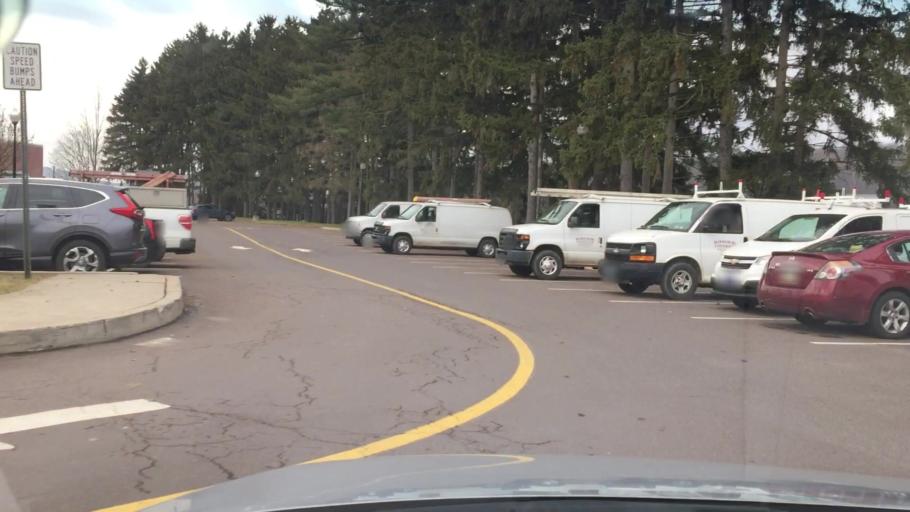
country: US
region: Pennsylvania
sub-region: Columbia County
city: Bloomsburg
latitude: 41.0092
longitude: -76.4473
